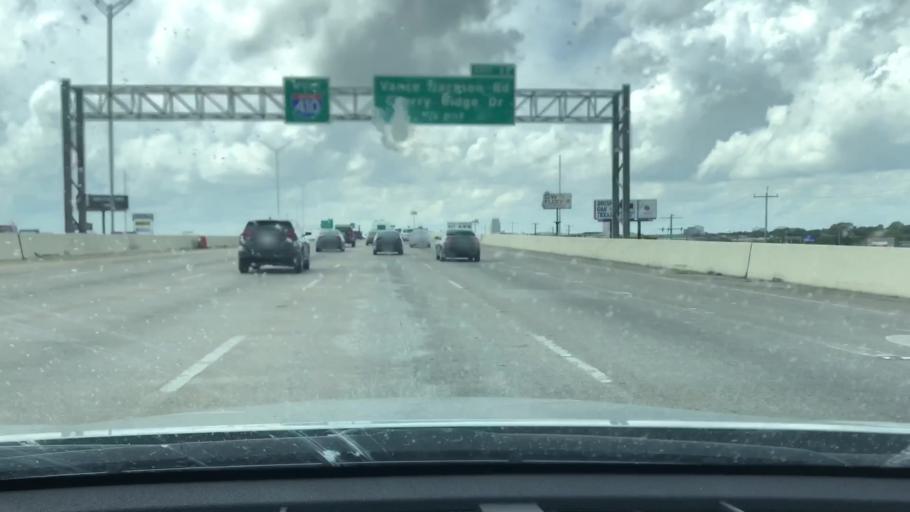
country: US
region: Texas
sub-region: Bexar County
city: Castle Hills
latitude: 29.5173
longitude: -98.5260
